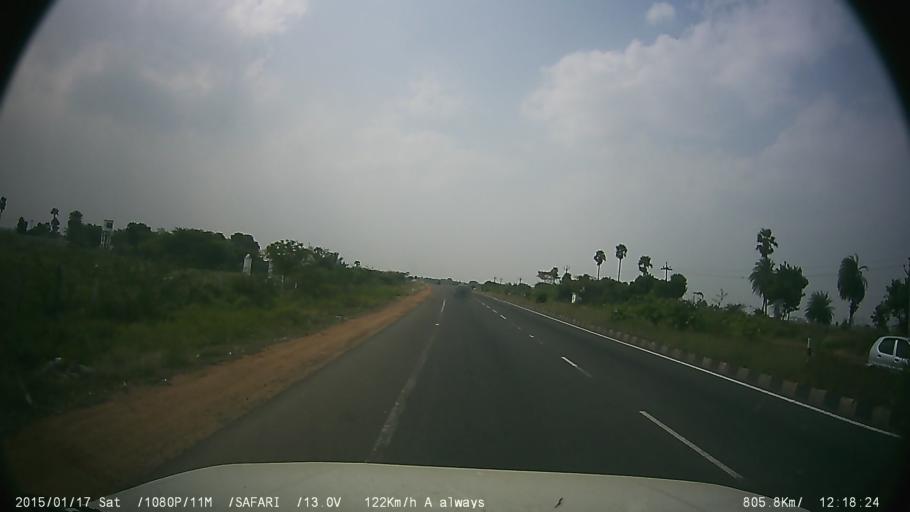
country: IN
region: Tamil Nadu
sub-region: Kancheepuram
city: Wallajahbad
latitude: 12.9066
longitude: 79.8289
